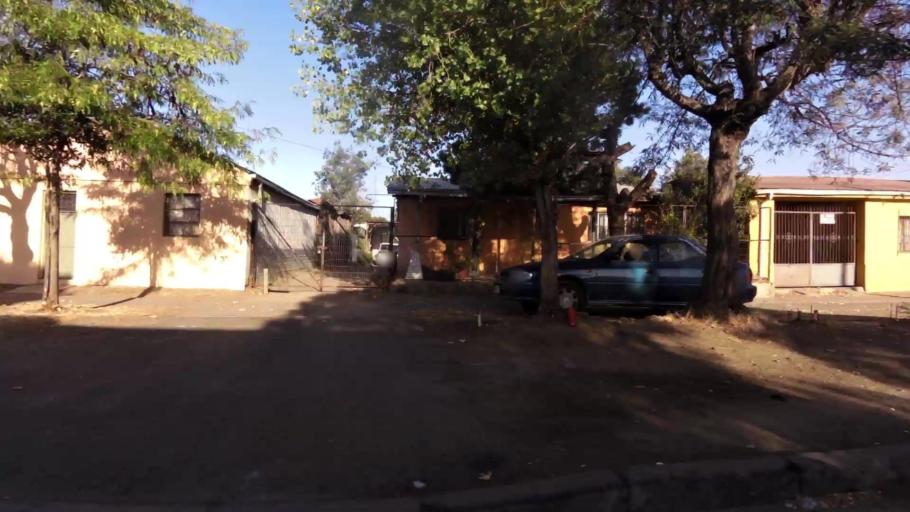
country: CL
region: Maule
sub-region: Provincia de Talca
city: Talca
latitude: -35.4377
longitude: -71.6488
